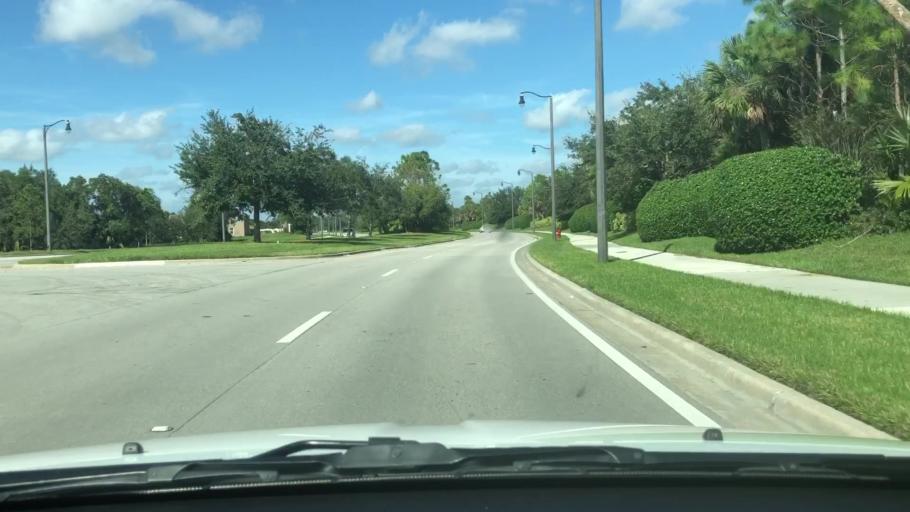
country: US
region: Florida
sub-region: Saint Lucie County
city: Port Saint Lucie
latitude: 27.2817
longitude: -80.4372
